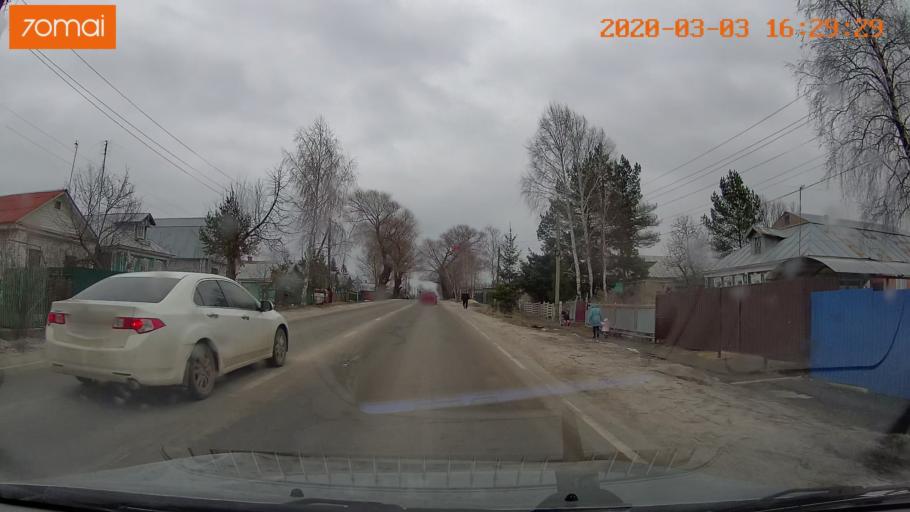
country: RU
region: Moskovskaya
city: Konobeyevo
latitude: 55.4367
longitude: 38.7011
